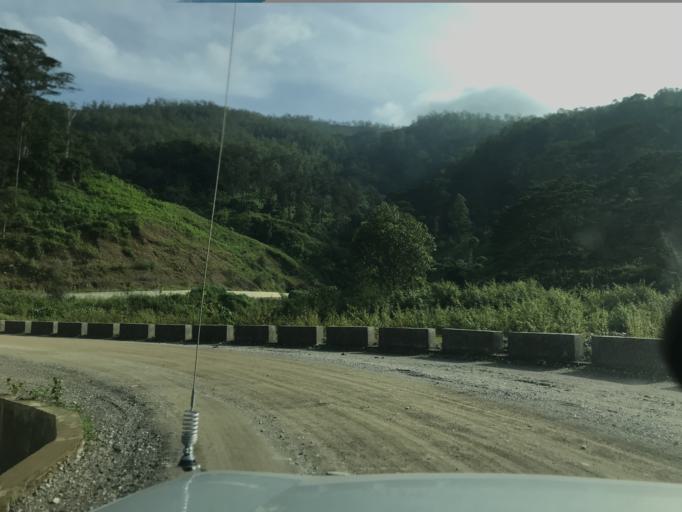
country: TL
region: Aileu
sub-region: Aileu Villa
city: Aileu
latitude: -8.6622
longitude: 125.5488
